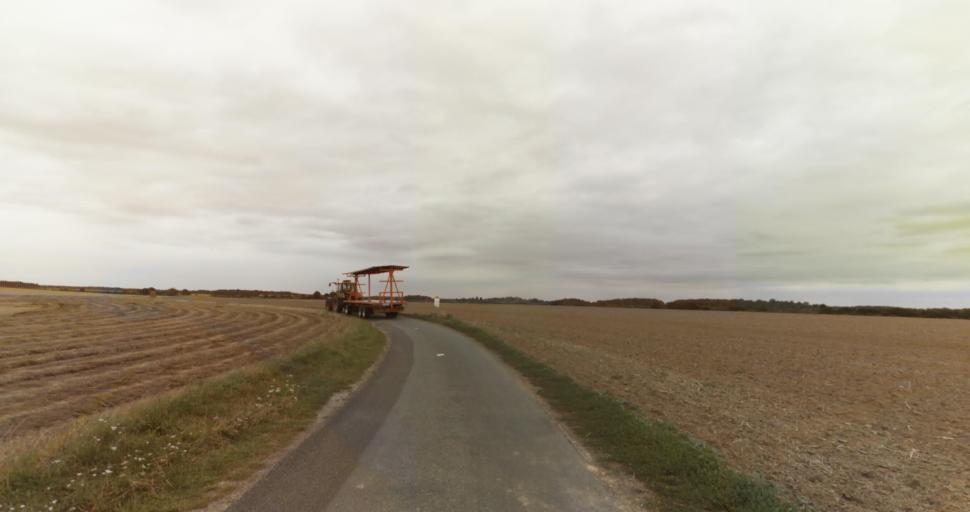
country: FR
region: Haute-Normandie
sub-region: Departement de l'Eure
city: Evreux
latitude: 48.9658
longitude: 1.2182
